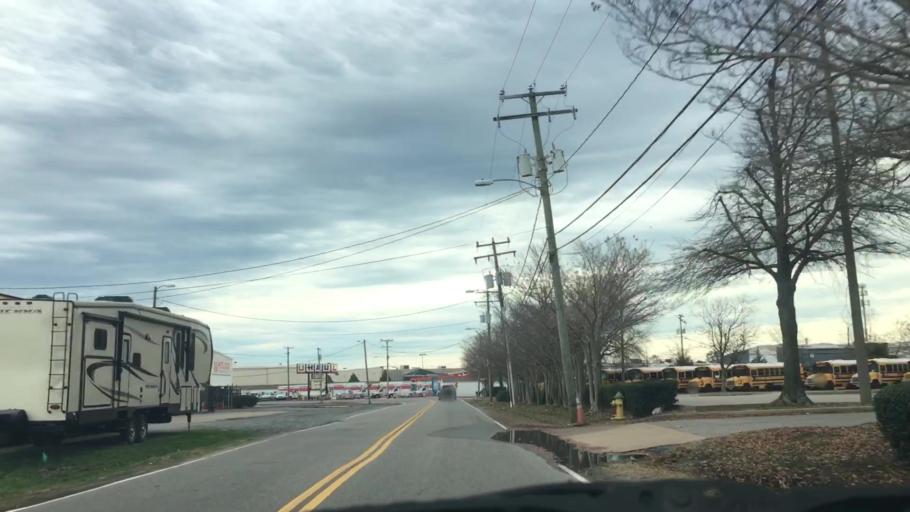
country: US
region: Virginia
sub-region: City of Norfolk
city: Norfolk
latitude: 36.8593
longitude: -76.2161
